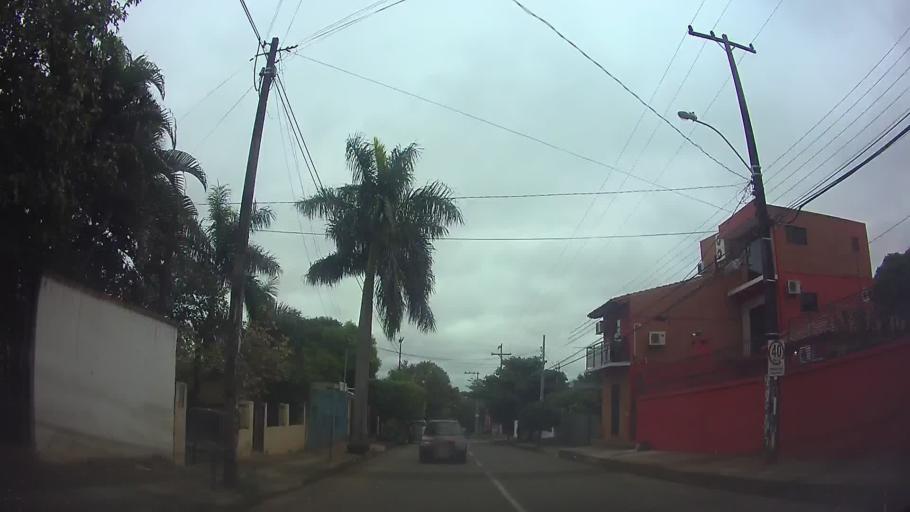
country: PY
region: Central
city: Lambare
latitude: -25.3329
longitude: -57.5806
